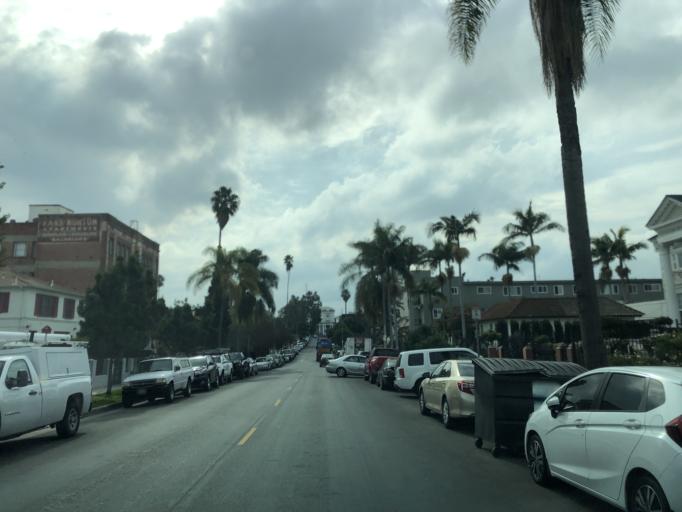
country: US
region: California
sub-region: Los Angeles County
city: Hollywood
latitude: 34.0502
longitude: -118.3226
